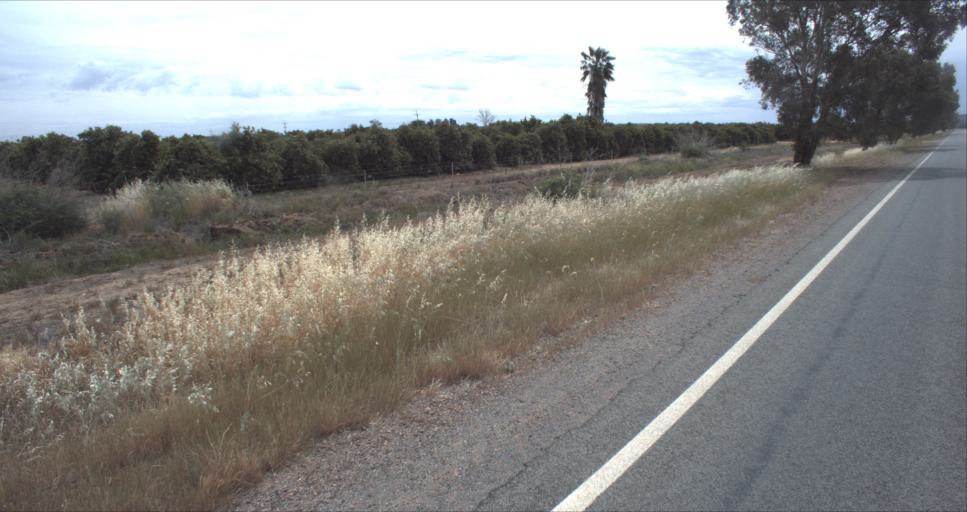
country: AU
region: New South Wales
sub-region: Leeton
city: Leeton
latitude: -34.5114
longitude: 146.4199
